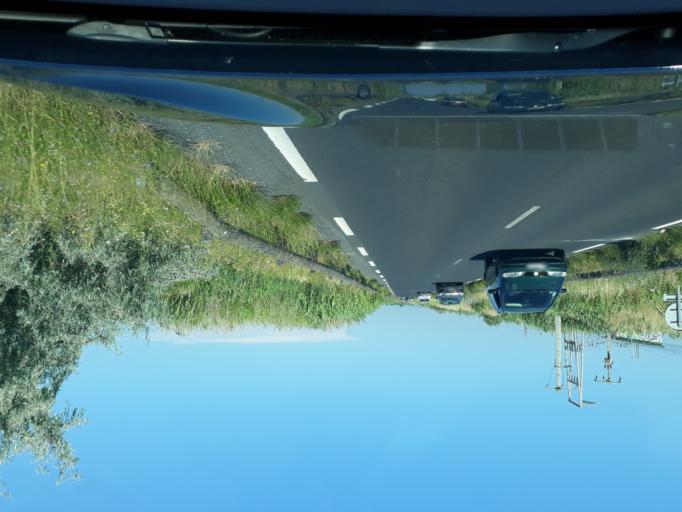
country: FR
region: Languedoc-Roussillon
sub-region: Departement de l'Herault
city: Marseillan
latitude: 43.3350
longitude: 3.5679
